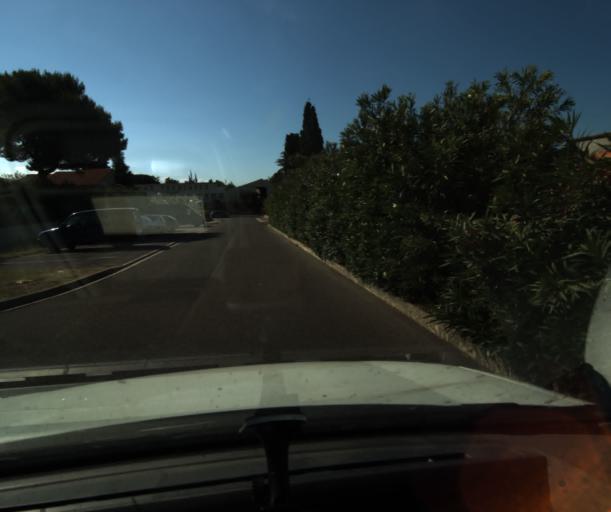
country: FR
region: Languedoc-Roussillon
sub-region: Departement des Pyrenees-Orientales
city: el Volo
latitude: 42.5268
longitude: 2.8359
